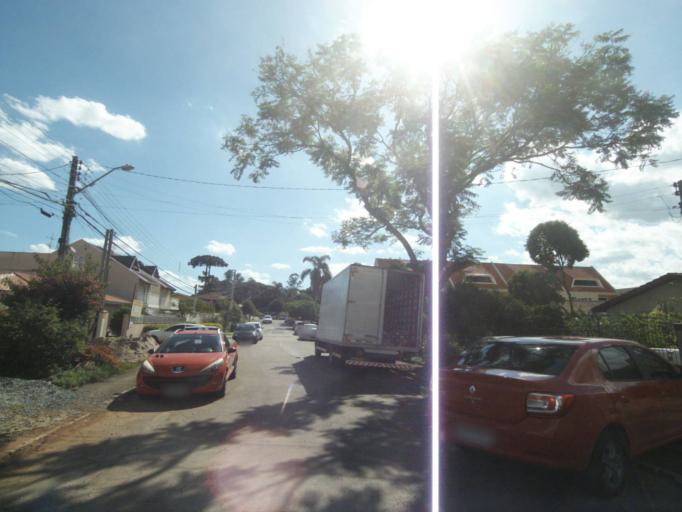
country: BR
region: Parana
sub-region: Curitiba
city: Curitiba
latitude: -25.4438
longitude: -49.3465
